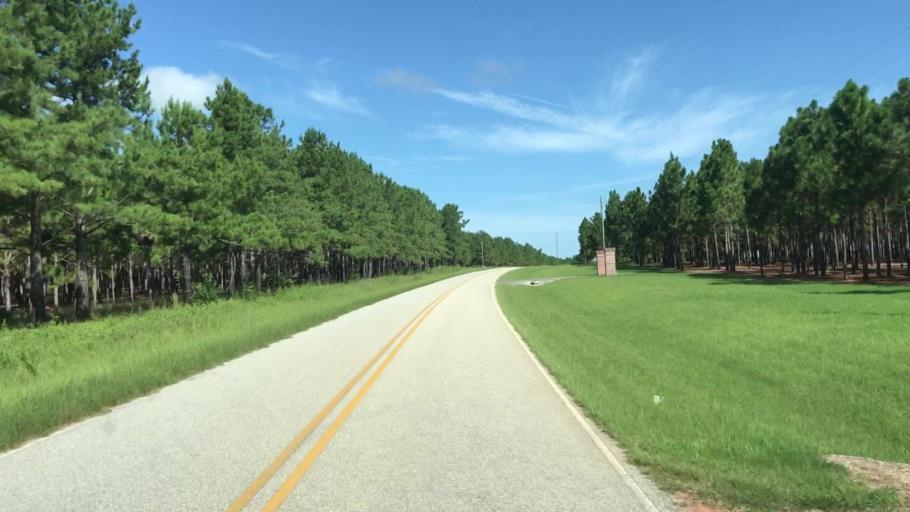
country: US
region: Georgia
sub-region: Jefferson County
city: Wadley
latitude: 32.8258
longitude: -82.3820
